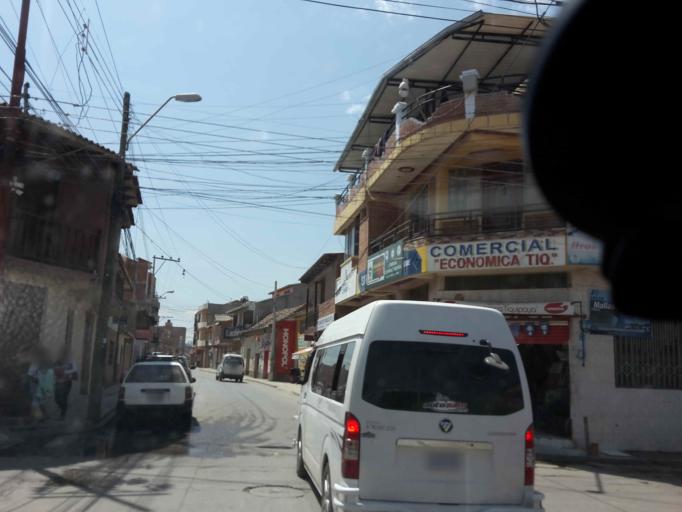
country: BO
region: Cochabamba
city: Cochabamba
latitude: -17.3394
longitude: -66.2195
